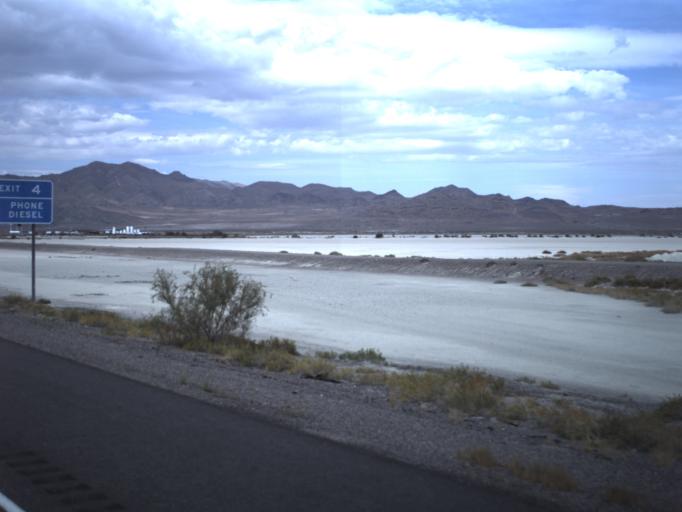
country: US
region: Utah
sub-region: Tooele County
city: Wendover
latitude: 40.7415
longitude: -113.9568
